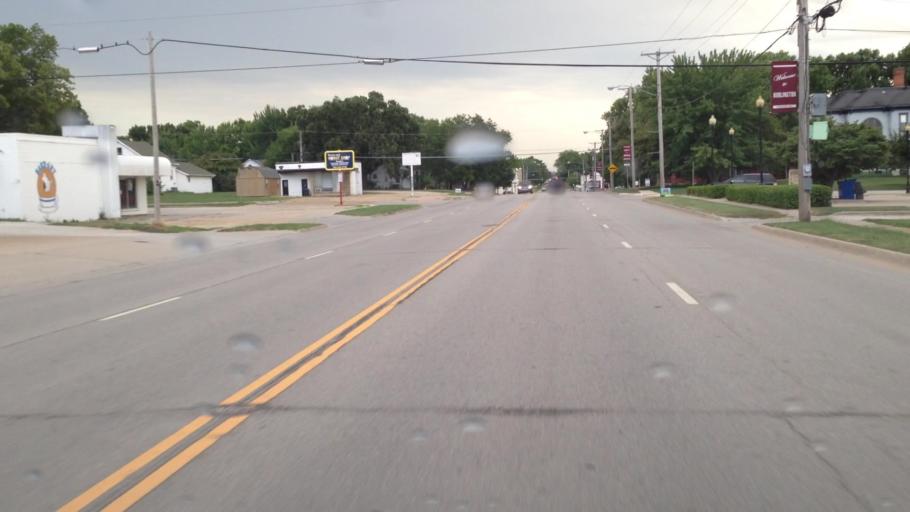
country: US
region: Kansas
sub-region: Coffey County
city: Burlington
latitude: 38.1983
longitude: -95.7386
